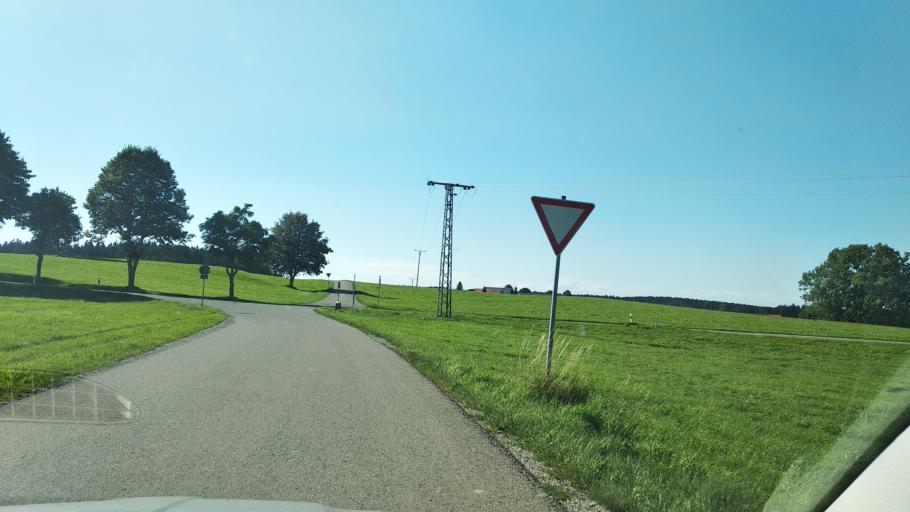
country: DE
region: Bavaria
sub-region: Swabia
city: Legau
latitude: 47.8310
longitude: 10.0859
